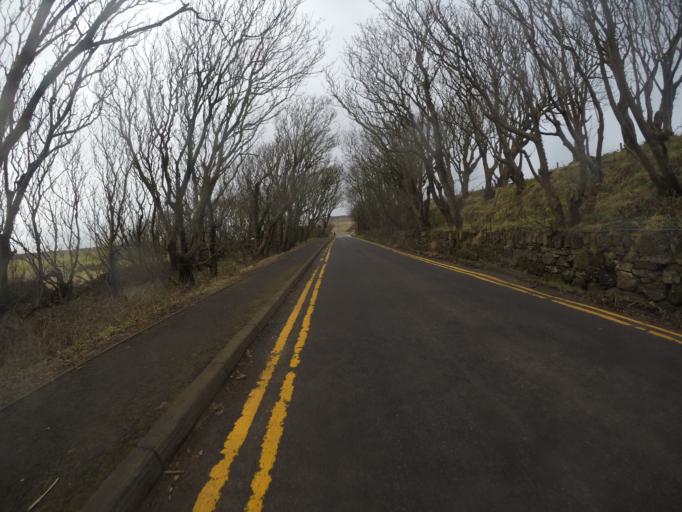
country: GB
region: Scotland
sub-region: North Ayrshire
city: West Kilbride
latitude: 55.6973
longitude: -4.8900
